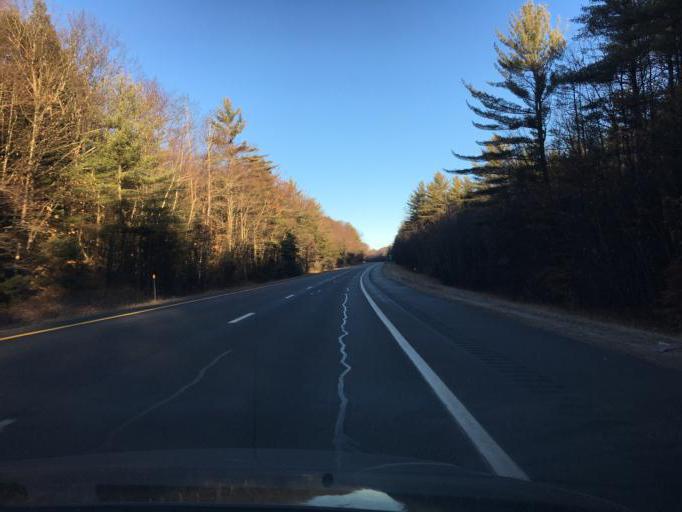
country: US
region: New Hampshire
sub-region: Belknap County
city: Sanbornton
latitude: 43.4846
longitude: -71.5922
